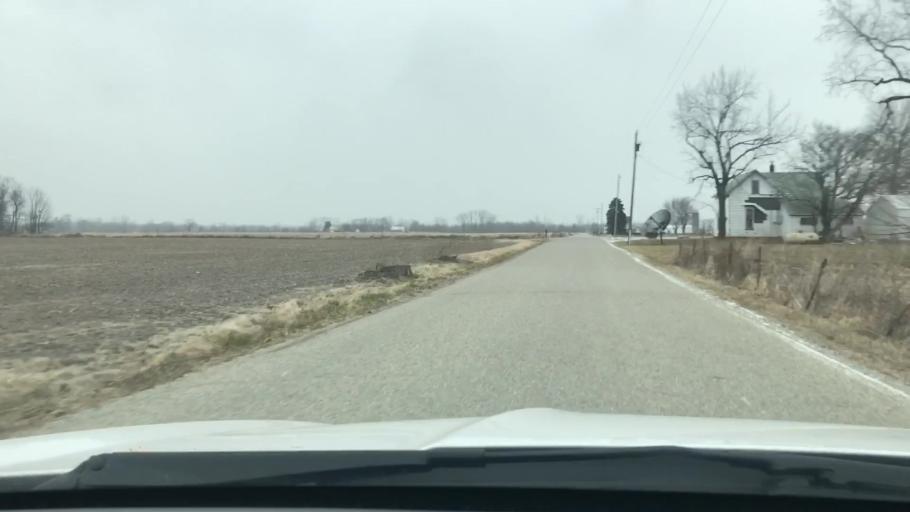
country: US
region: Indiana
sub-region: Fulton County
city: Akron
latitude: 41.0394
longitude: -86.0953
